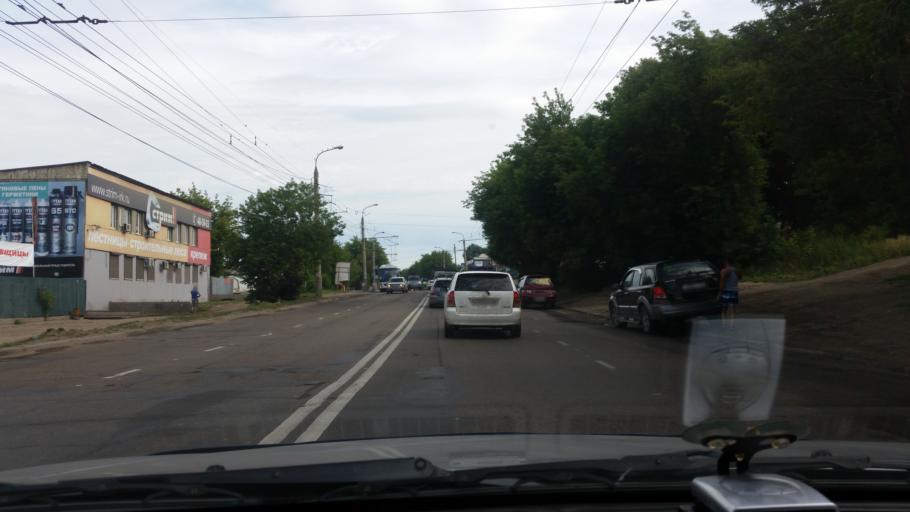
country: RU
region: Irkutsk
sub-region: Irkutskiy Rayon
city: Irkutsk
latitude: 52.3162
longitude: 104.3016
